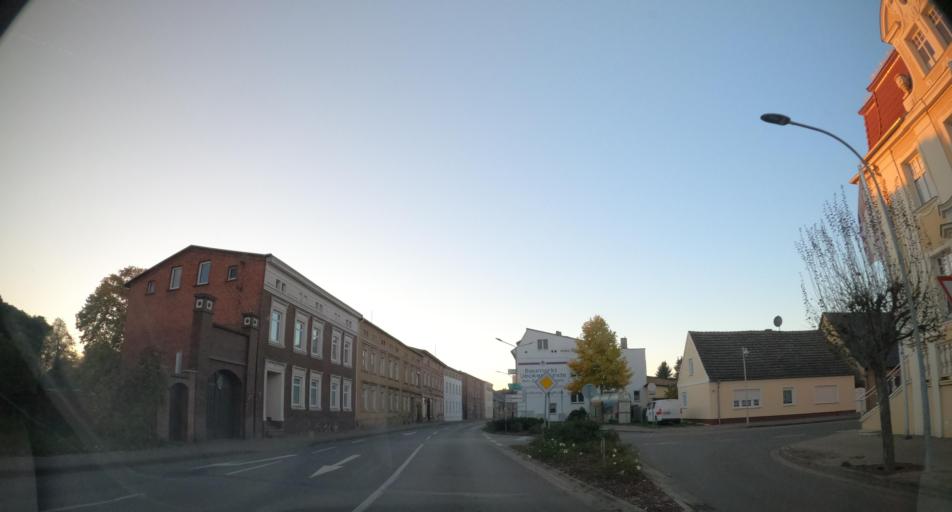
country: DE
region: Mecklenburg-Vorpommern
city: Ueckermunde
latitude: 53.7391
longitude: 14.0413
